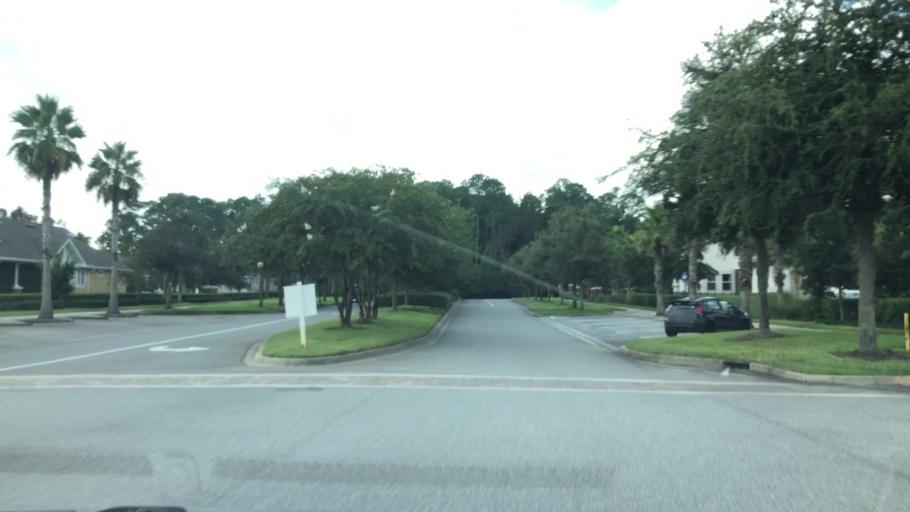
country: US
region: Florida
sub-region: Saint Johns County
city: Palm Valley
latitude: 30.1065
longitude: -81.4212
